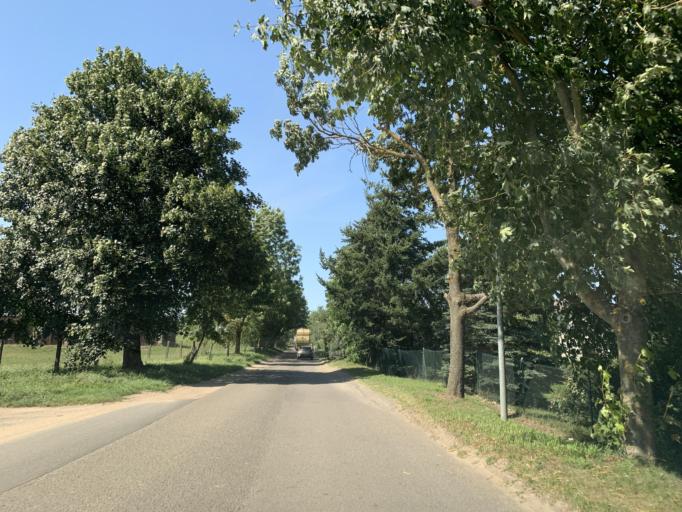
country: DE
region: Mecklenburg-Vorpommern
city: Loitz
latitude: 53.3587
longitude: 13.3889
